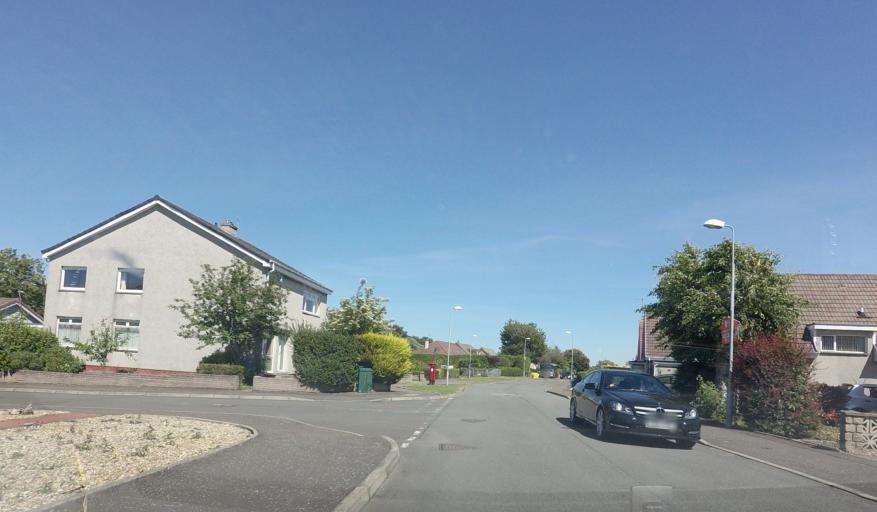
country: GB
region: Scotland
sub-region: West Lothian
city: Broxburn
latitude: 55.9321
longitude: -3.4752
